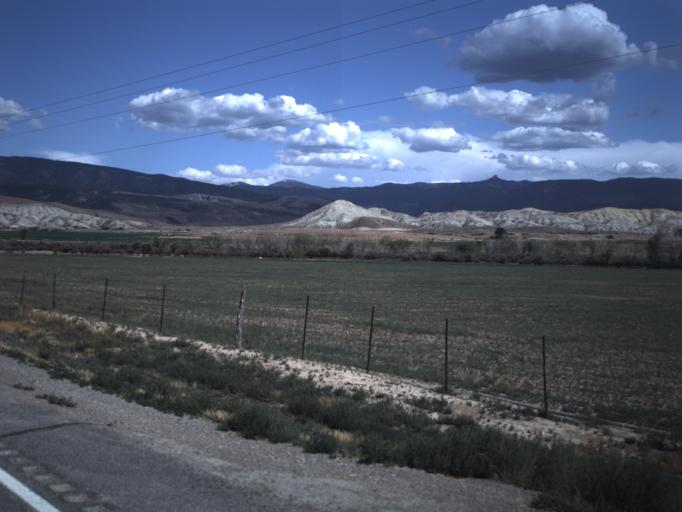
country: US
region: Utah
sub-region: Sanpete County
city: Gunnison
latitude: 39.1554
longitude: -111.7649
